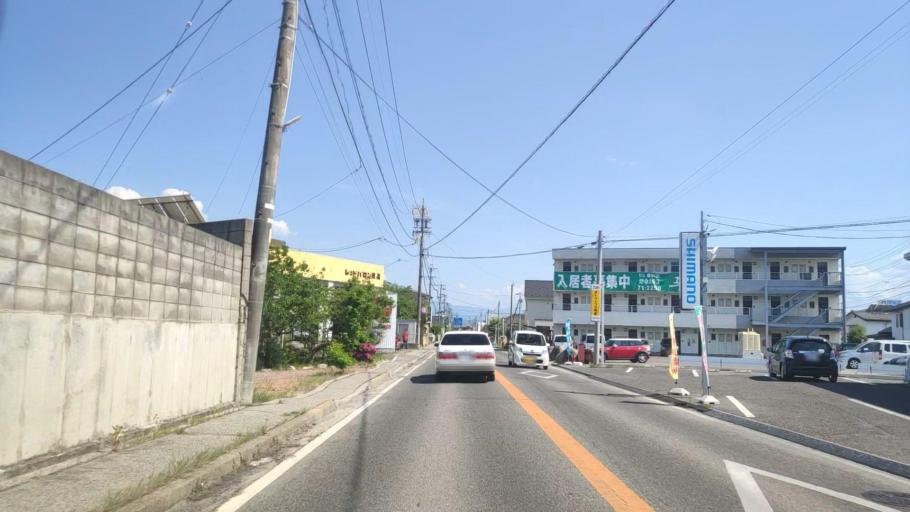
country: JP
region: Nagano
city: Hotaka
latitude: 36.3477
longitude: 137.8838
